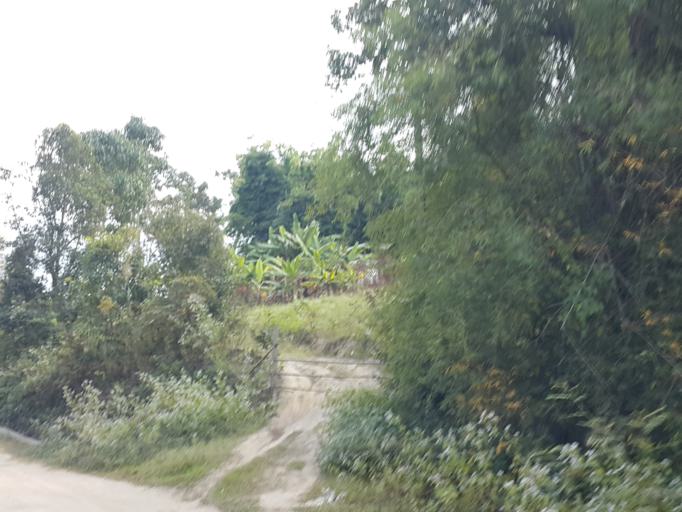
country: TH
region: Chiang Mai
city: Om Koi
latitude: 17.8106
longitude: 98.3180
